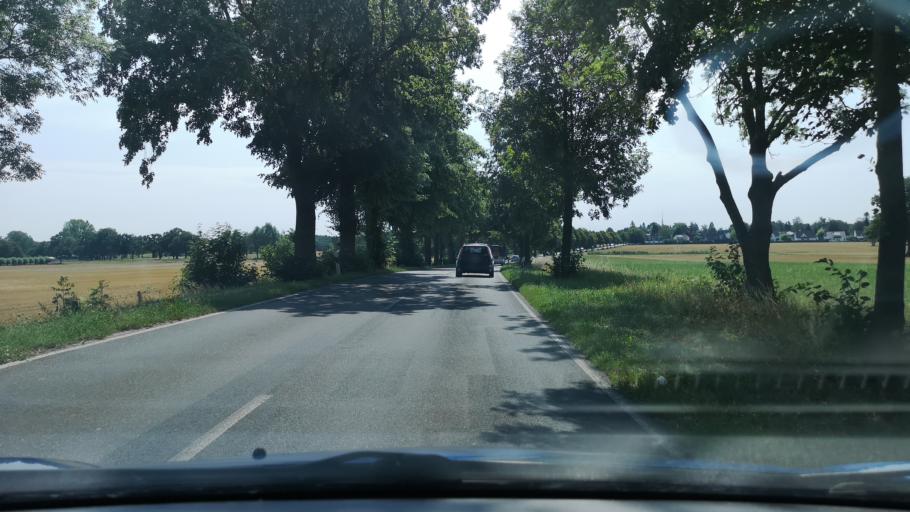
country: DE
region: Lower Saxony
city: Isernhagen Farster Bauerschaft
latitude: 52.4532
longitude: 9.7989
